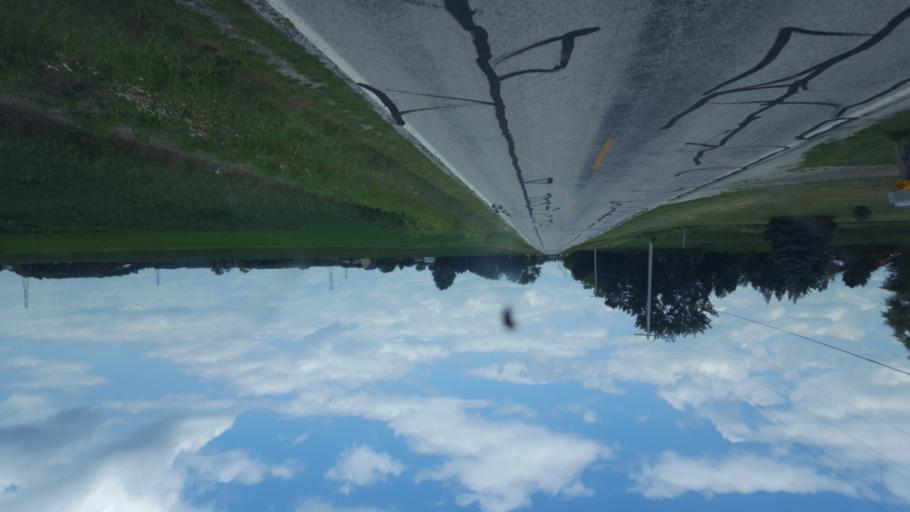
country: US
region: Ohio
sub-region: Lucas County
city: Curtice
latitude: 41.5982
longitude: -83.2804
